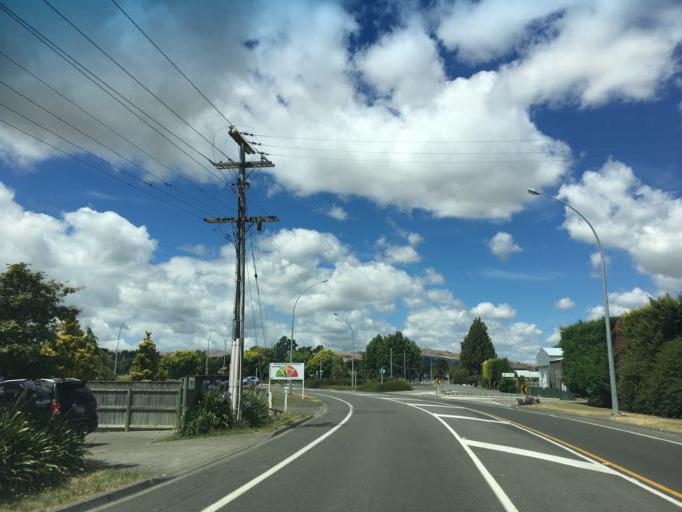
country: NZ
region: Hawke's Bay
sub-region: Hastings District
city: Hastings
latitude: -39.6579
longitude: 176.8862
